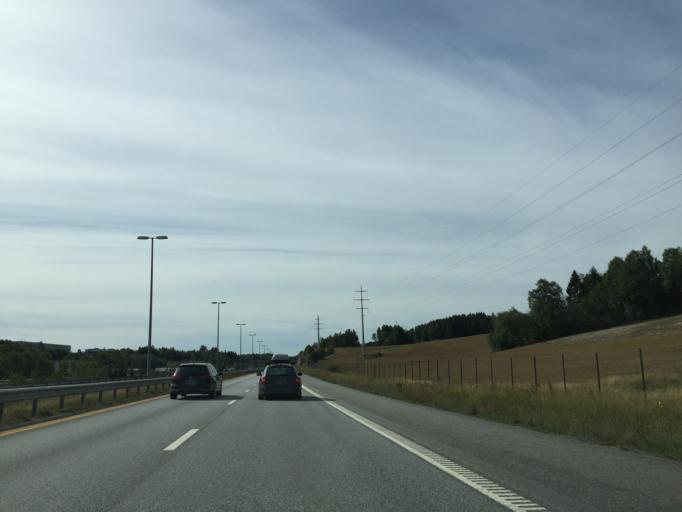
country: NO
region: Akershus
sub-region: Vestby
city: Vestby
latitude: 59.5910
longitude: 10.7375
